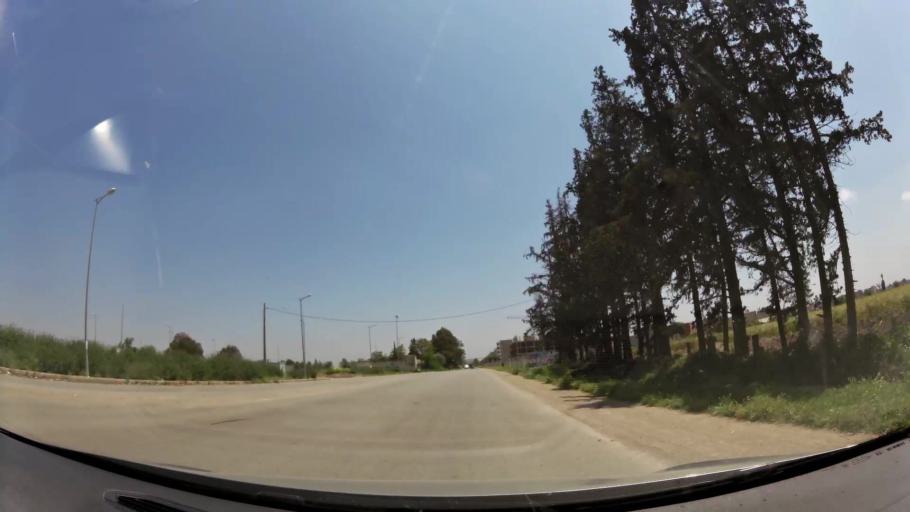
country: MA
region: Fes-Boulemane
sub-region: Fes
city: Fes
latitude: 34.0283
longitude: -5.0573
